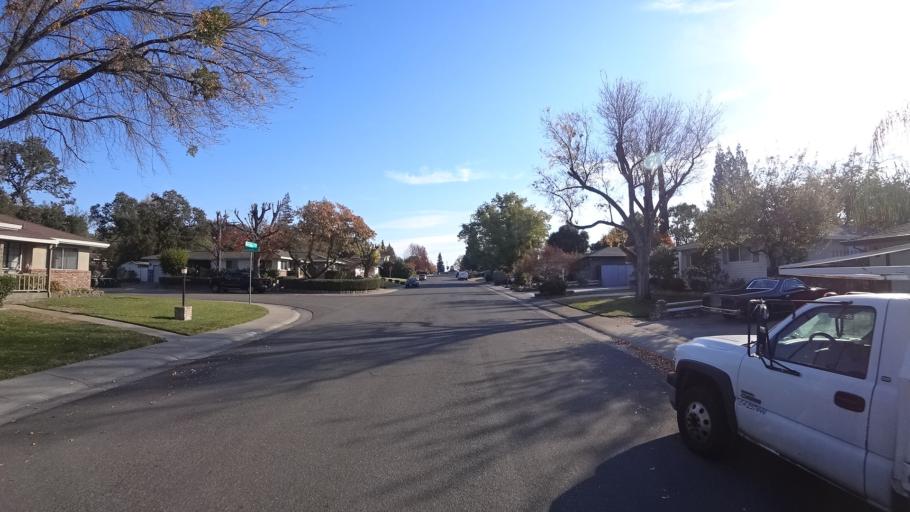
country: US
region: California
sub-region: Sacramento County
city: Citrus Heights
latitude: 38.6806
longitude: -121.3034
